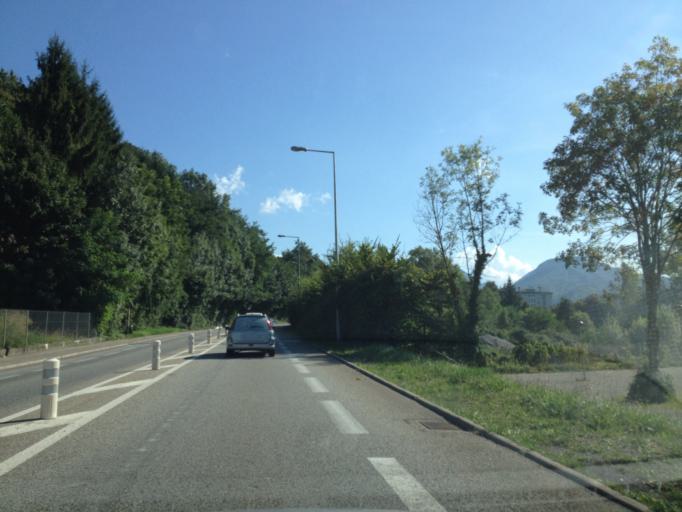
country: FR
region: Rhone-Alpes
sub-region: Departement de la Savoie
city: Cognin
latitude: 45.5673
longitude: 5.9035
